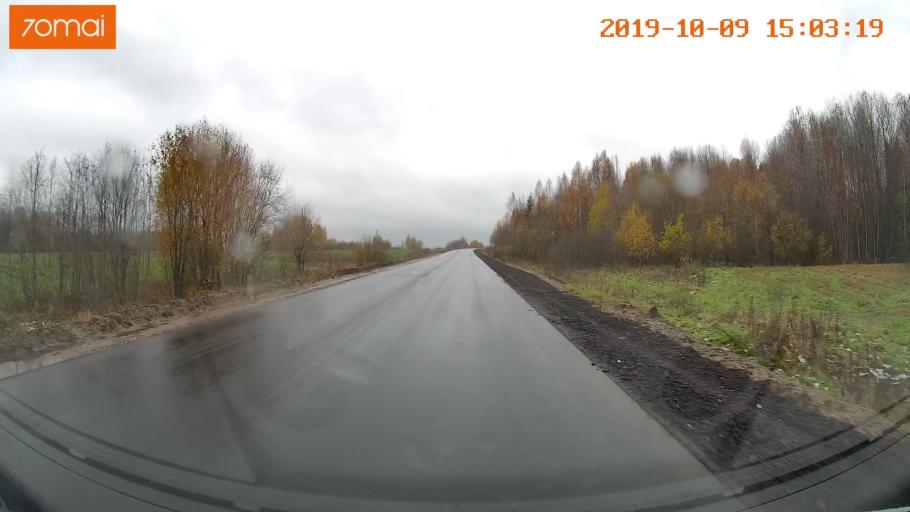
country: RU
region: Kostroma
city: Chistyye Bory
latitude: 58.2729
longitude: 41.6760
